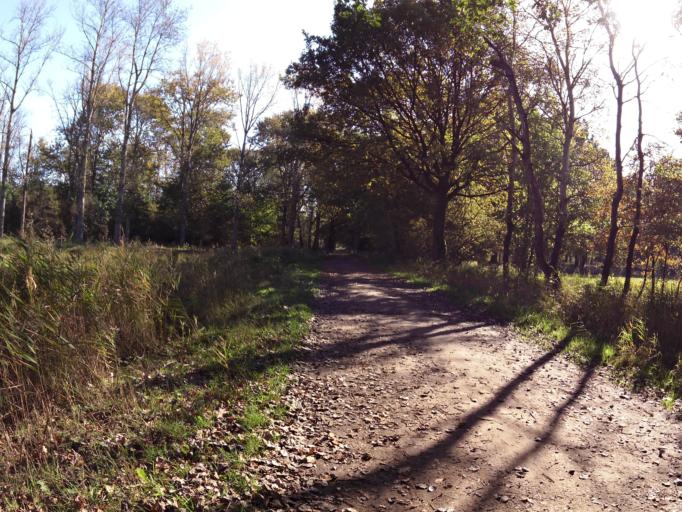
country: NL
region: Limburg
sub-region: Gemeente Weert
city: Weert
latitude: 51.3067
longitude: 5.6715
